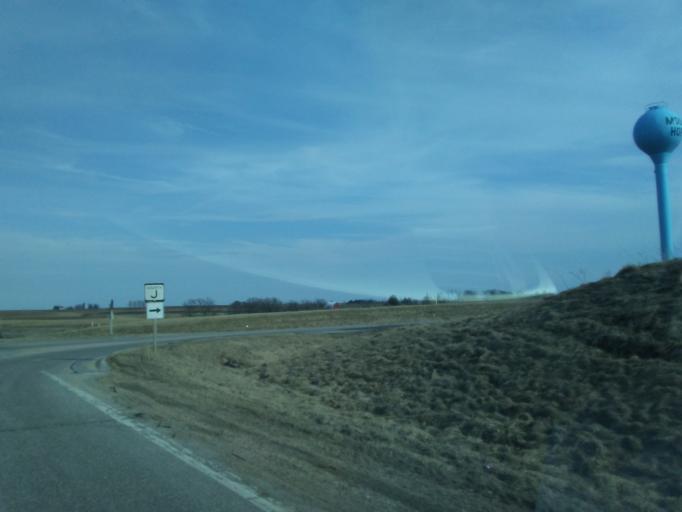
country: US
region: Wisconsin
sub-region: Grant County
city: Lancaster
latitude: 42.9741
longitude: -90.8595
